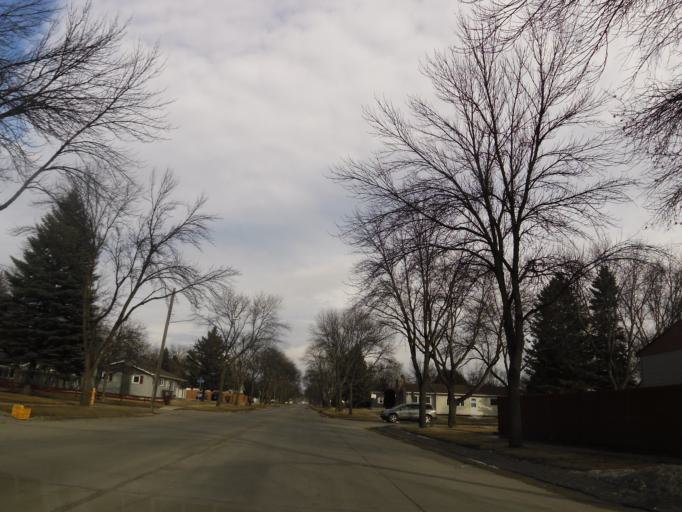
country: US
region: North Dakota
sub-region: Grand Forks County
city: Grand Forks
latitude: 47.9092
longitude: -97.0548
